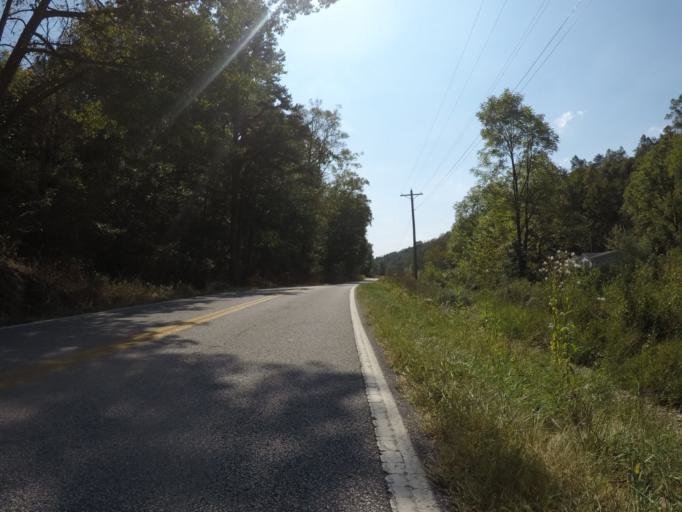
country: US
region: West Virginia
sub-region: Cabell County
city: Lesage
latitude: 38.5738
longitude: -82.4048
